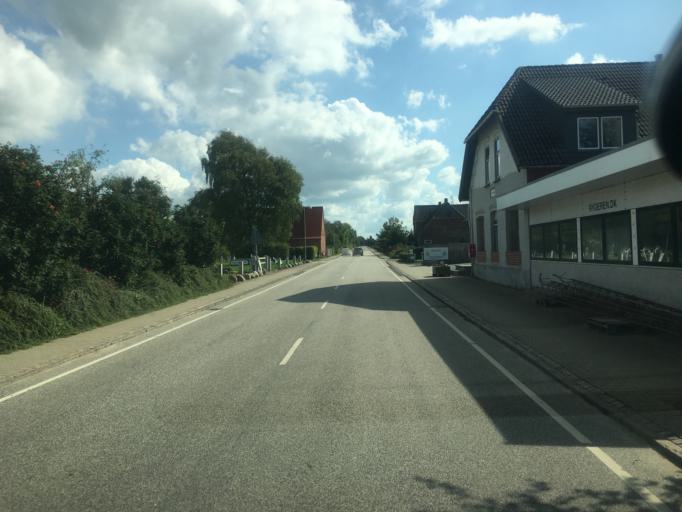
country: DE
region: Schleswig-Holstein
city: Ellhoft
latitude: 54.9411
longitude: 8.9684
